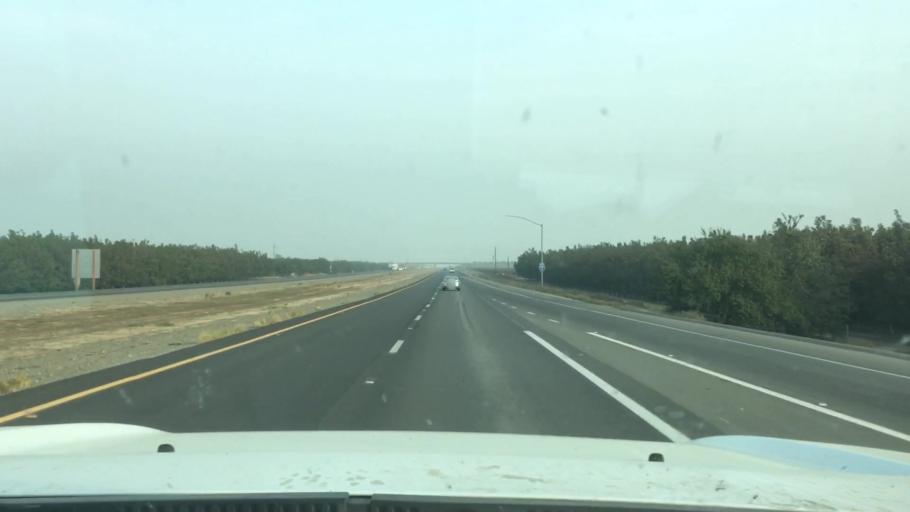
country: US
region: California
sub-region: San Joaquin County
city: Tracy
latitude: 37.6863
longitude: -121.3430
